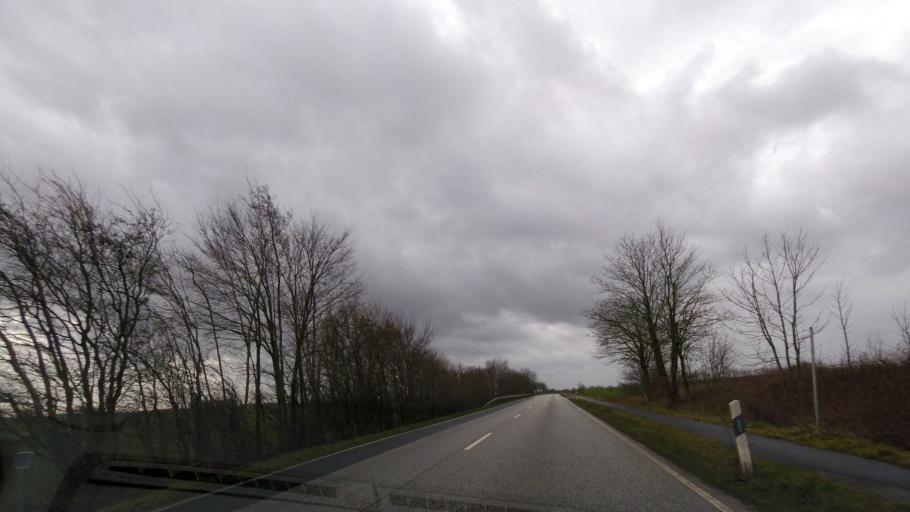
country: DE
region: Schleswig-Holstein
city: Loit
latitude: 54.6076
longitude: 9.6969
